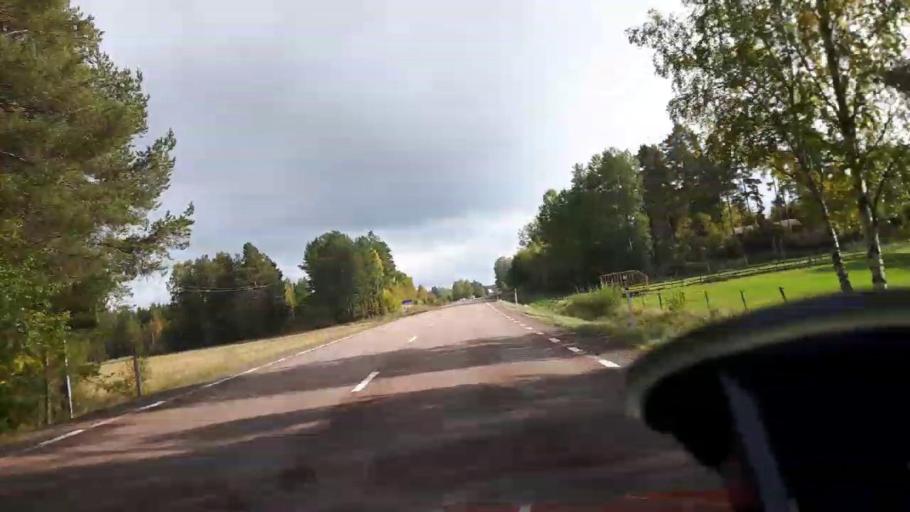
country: SE
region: Gaevleborg
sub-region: Soderhamns Kommun
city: Soderhamn
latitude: 61.1654
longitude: 16.8504
